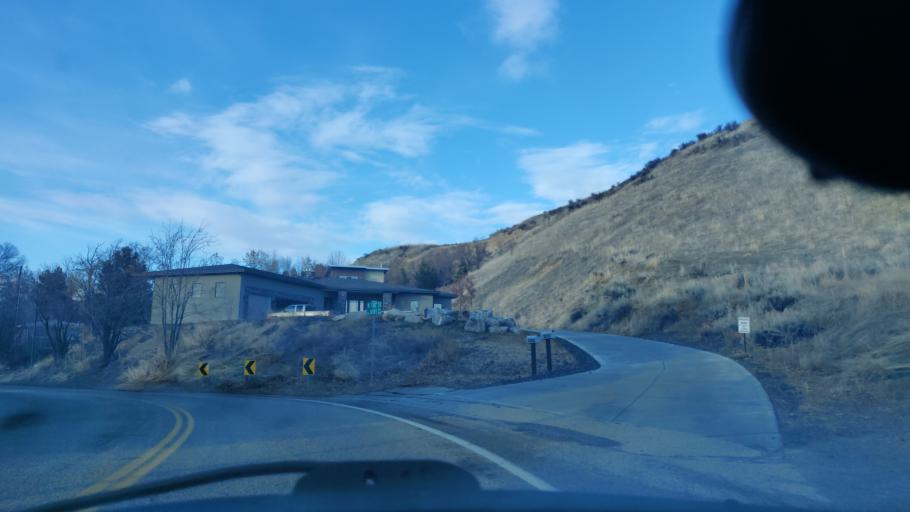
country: US
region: Idaho
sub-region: Ada County
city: Boise
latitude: 43.6364
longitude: -116.2033
